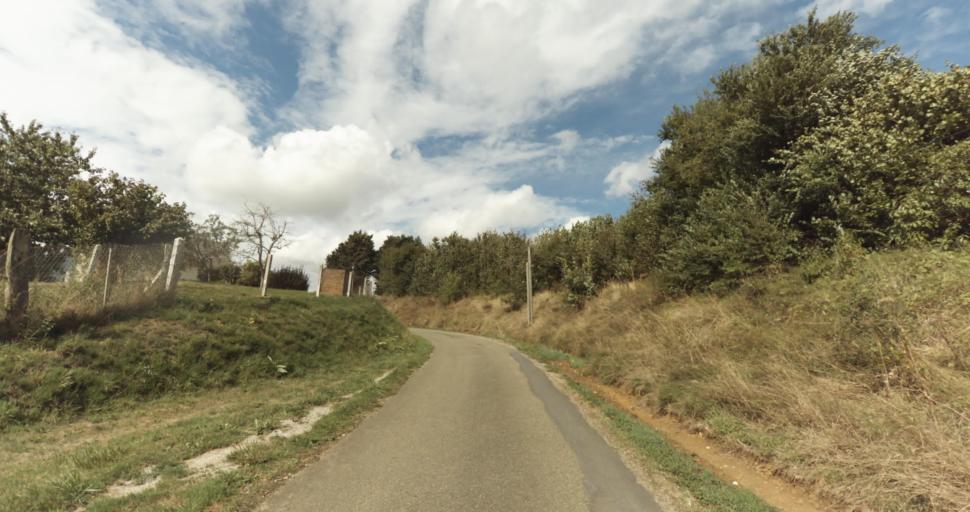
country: FR
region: Lower Normandy
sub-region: Departement de l'Orne
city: Gace
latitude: 48.7723
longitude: 0.3102
